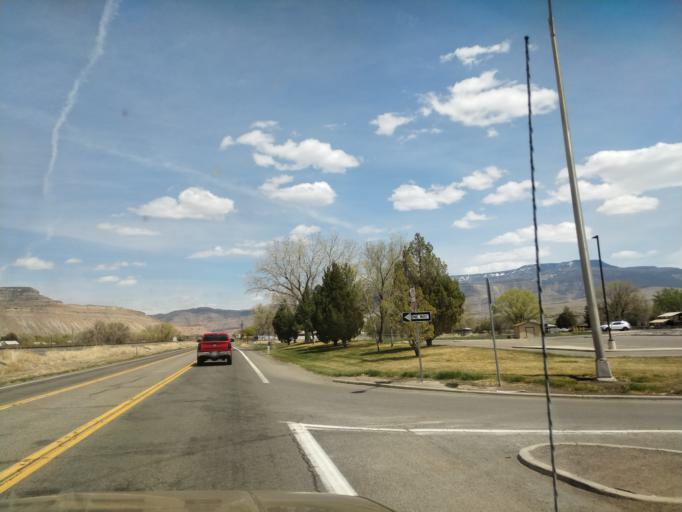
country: US
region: Colorado
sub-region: Mesa County
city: Clifton
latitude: 39.0979
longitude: -108.4080
